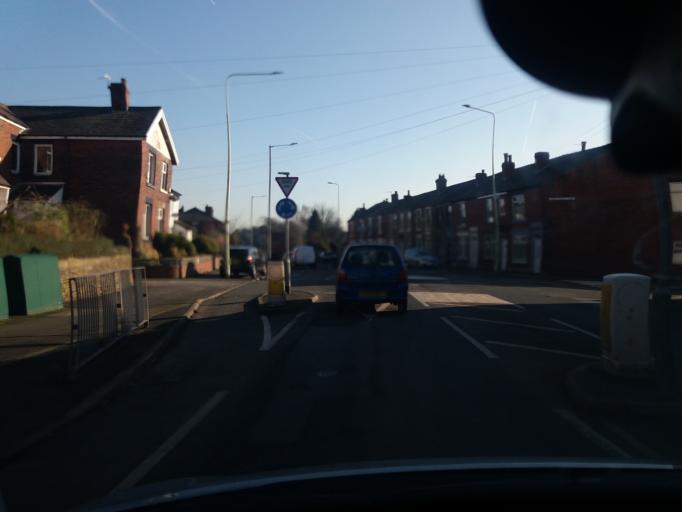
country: GB
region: England
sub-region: Lancashire
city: Adlington
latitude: 53.6229
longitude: -2.6058
